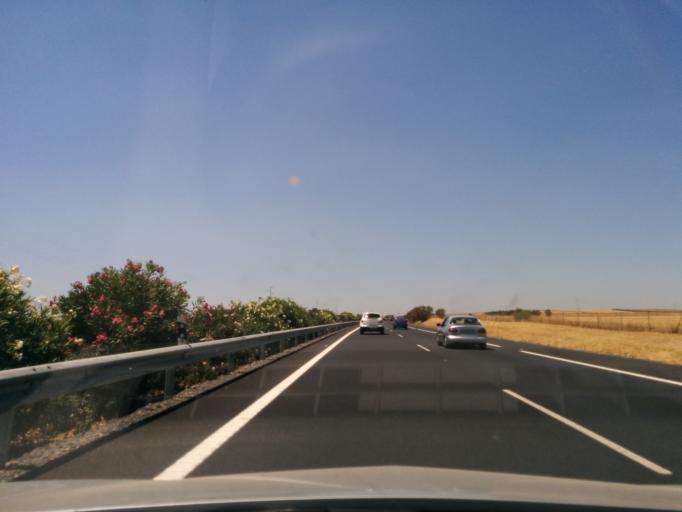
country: ES
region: Andalusia
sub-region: Provincia de Huelva
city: San Juan del Puerto
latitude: 37.3305
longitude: -6.8120
